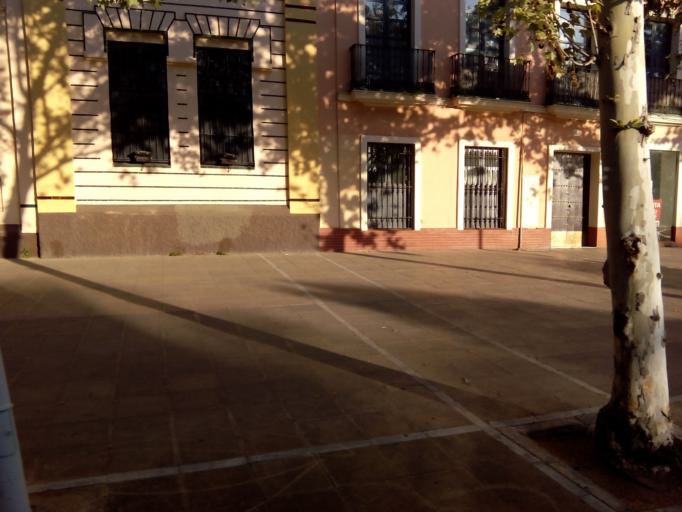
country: ES
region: Andalusia
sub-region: Provincia de Sevilla
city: Sevilla
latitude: 37.4009
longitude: -5.9981
